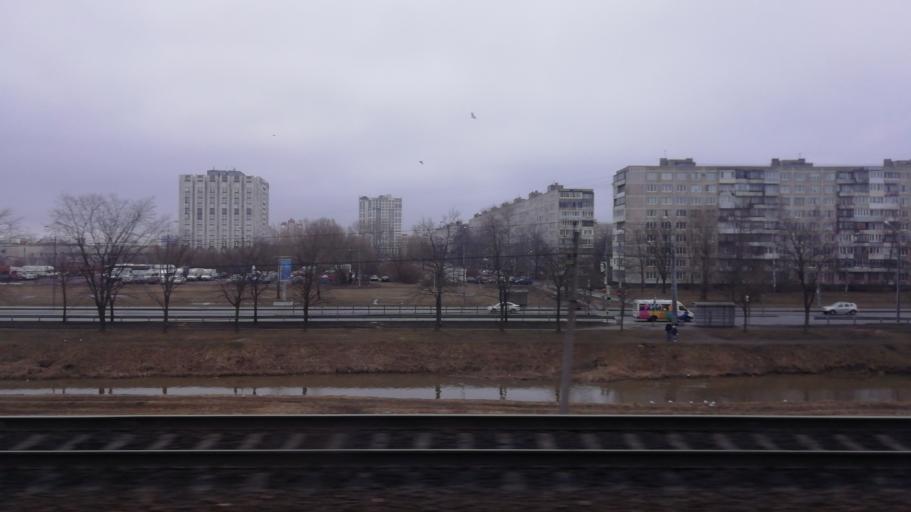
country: RU
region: St.-Petersburg
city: Kupchino
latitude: 59.8718
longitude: 30.3556
